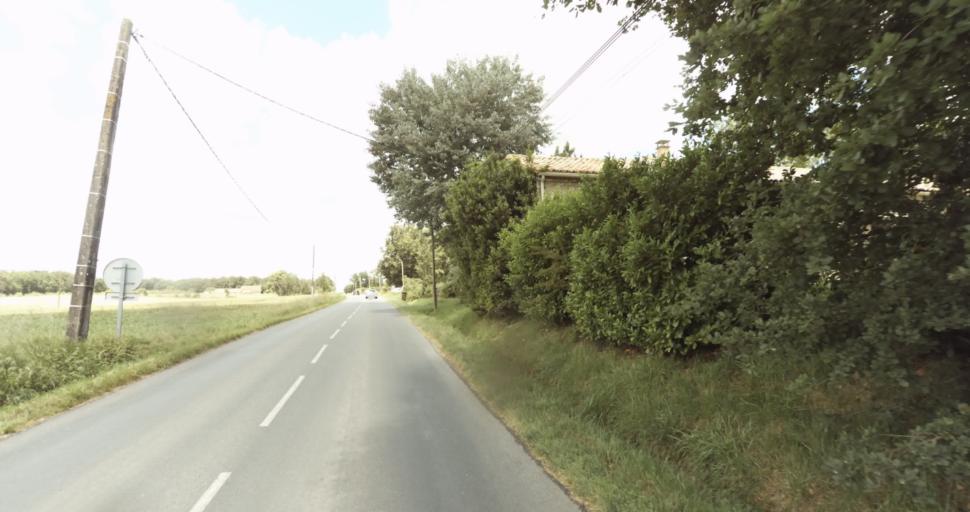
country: FR
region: Aquitaine
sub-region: Departement de la Dordogne
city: Beaumont-du-Perigord
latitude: 44.7282
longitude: 0.7575
